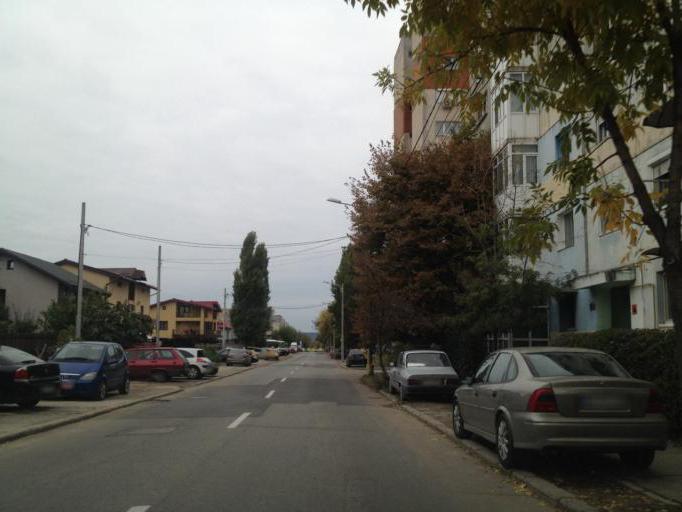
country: RO
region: Dolj
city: Craiova
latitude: 44.3340
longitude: 23.7843
